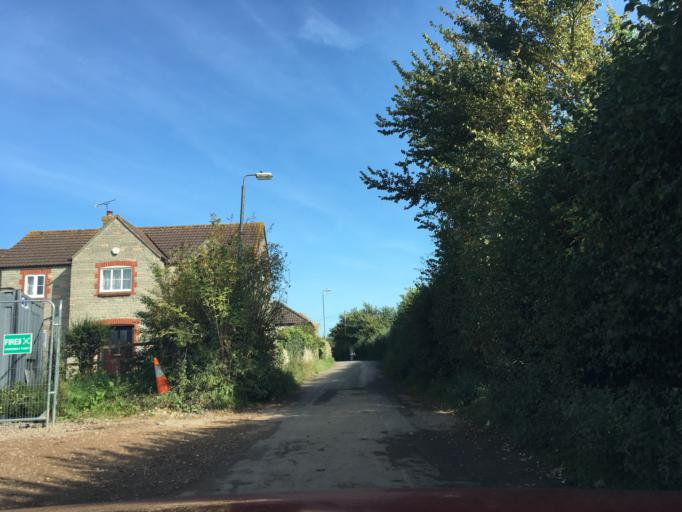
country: GB
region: England
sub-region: South Gloucestershire
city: Falfield
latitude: 51.6131
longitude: -2.4389
